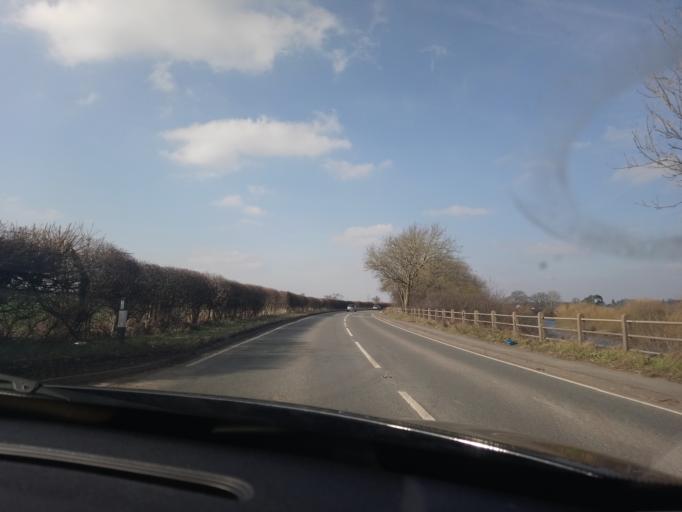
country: GB
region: England
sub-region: Shropshire
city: Berrington
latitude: 52.6817
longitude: -2.6893
